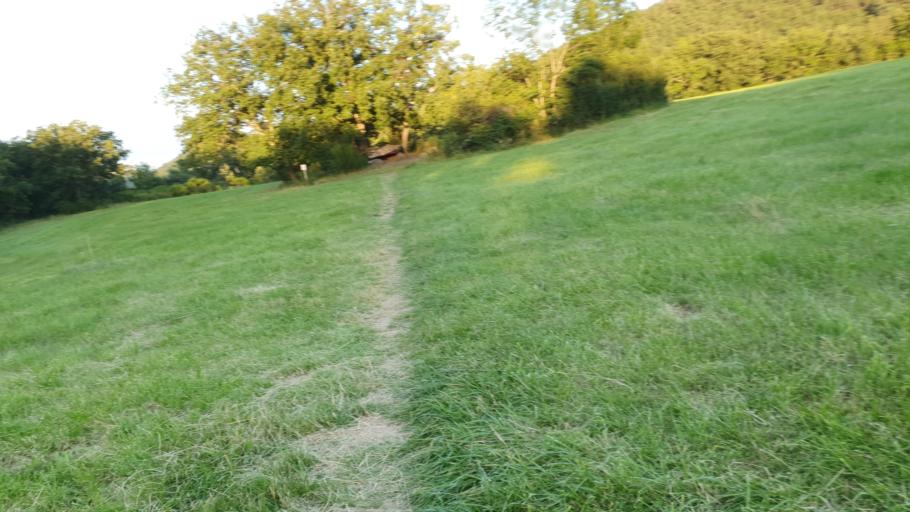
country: FR
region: Auvergne
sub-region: Departement du Puy-de-Dome
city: Aydat
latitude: 45.5699
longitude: 3.0195
